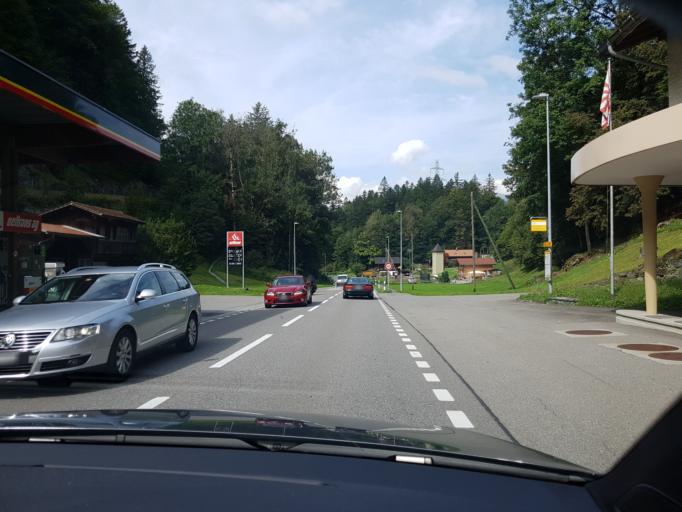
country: CH
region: Bern
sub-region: Interlaken-Oberhasli District
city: Meiringen
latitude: 46.7149
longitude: 8.2102
